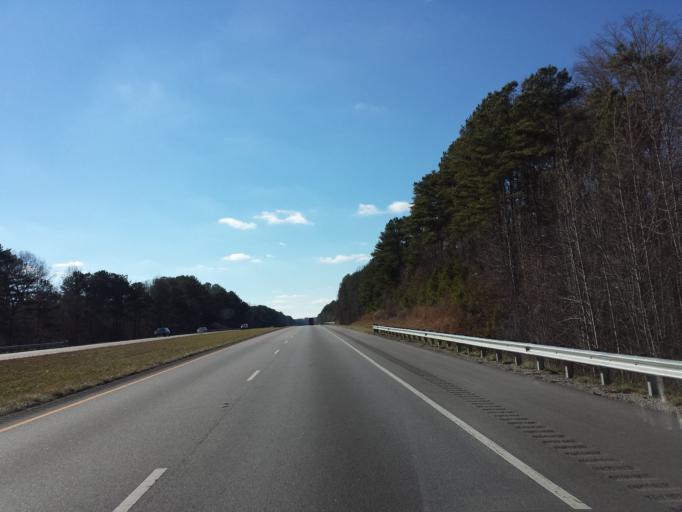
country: US
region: Alabama
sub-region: Cleburne County
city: Heflin
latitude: 33.6278
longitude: -85.5600
